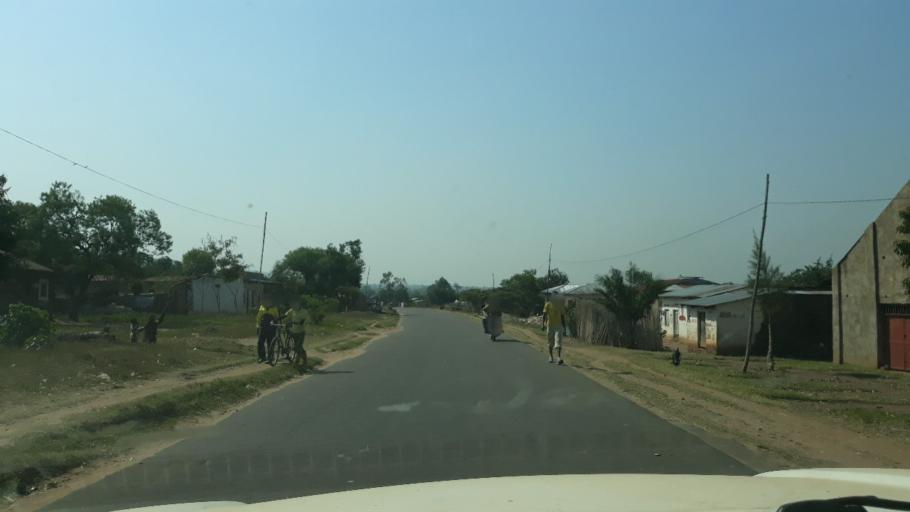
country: CD
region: South Kivu
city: Uvira
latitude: -3.2308
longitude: 29.1660
